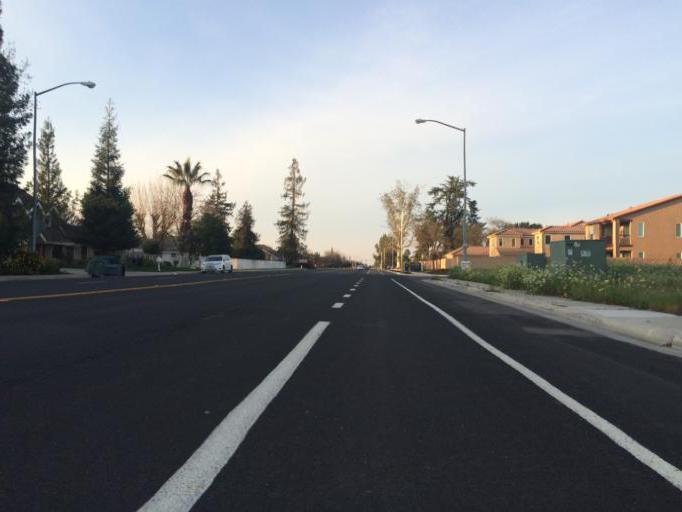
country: US
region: California
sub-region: Fresno County
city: Tarpey Village
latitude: 36.7957
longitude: -119.6730
